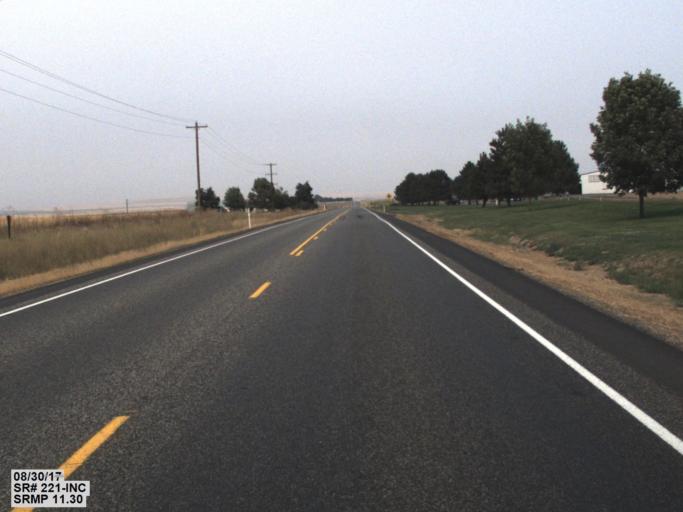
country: US
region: Washington
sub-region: Benton County
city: Prosser
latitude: 46.0988
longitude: -119.6018
